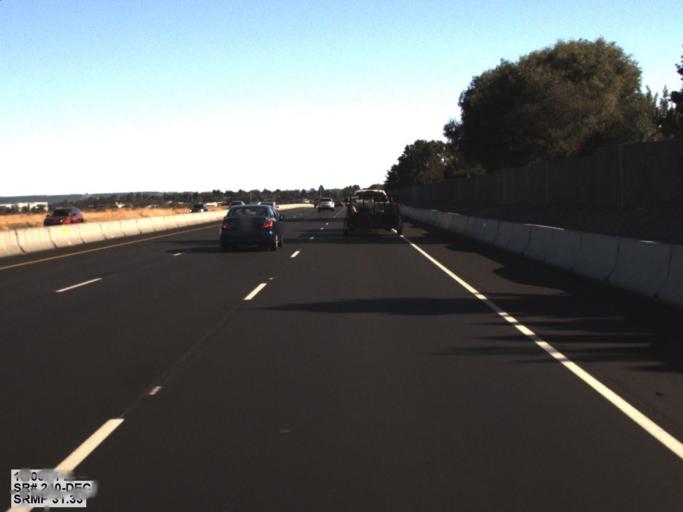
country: US
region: Washington
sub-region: Benton County
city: Richland
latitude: 46.3011
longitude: -119.2958
